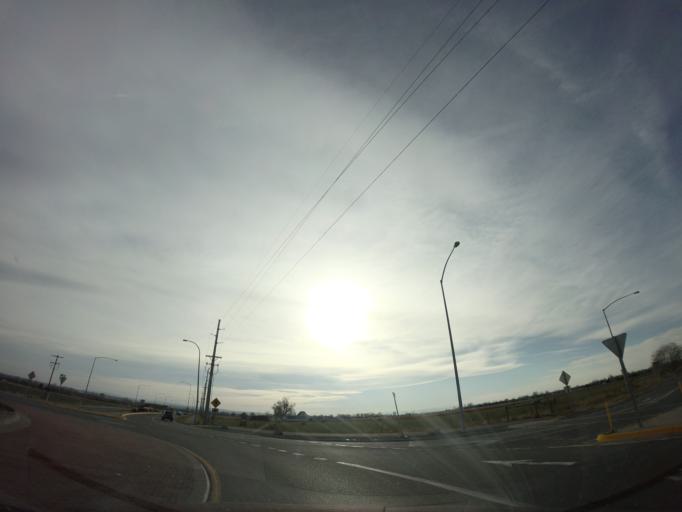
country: US
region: Montana
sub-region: Yellowstone County
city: Billings
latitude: 45.7839
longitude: -108.6177
